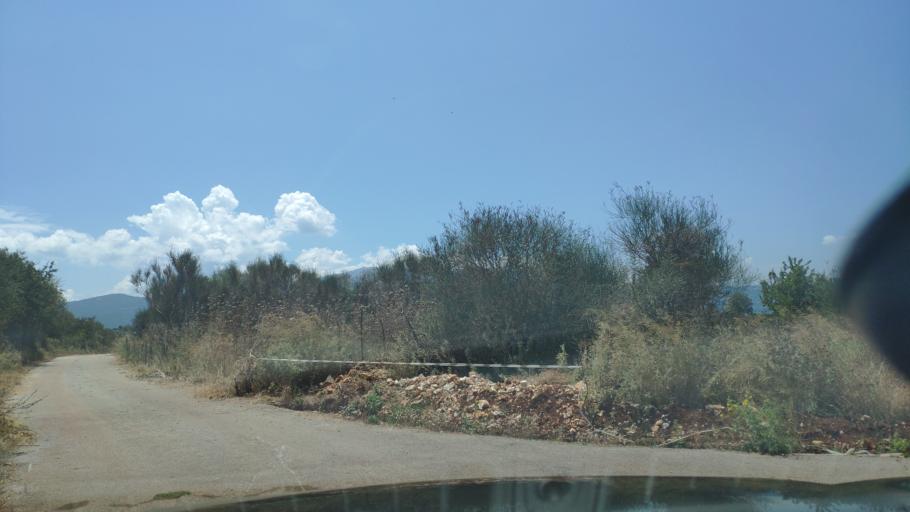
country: GR
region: West Greece
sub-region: Nomos Aitolias kai Akarnanias
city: Amfilochia
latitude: 38.9060
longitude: 21.0990
